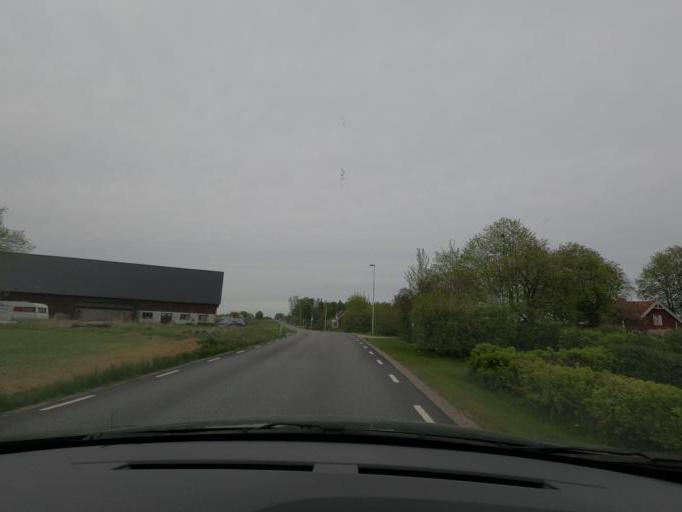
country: SE
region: Joenkoeping
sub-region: Varnamo Kommun
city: Bredaryd
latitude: 57.1339
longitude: 13.7084
